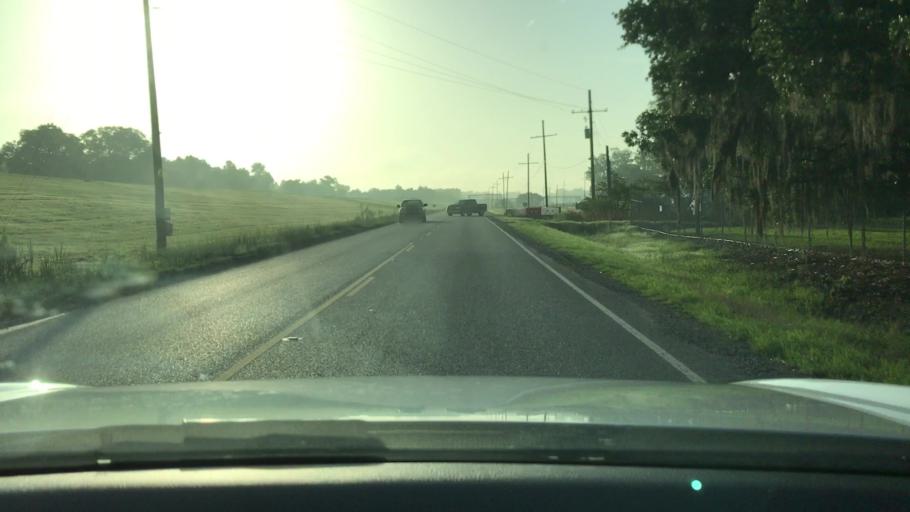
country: US
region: Louisiana
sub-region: Iberville Parish
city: Plaquemine
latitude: 30.2734
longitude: -91.1787
